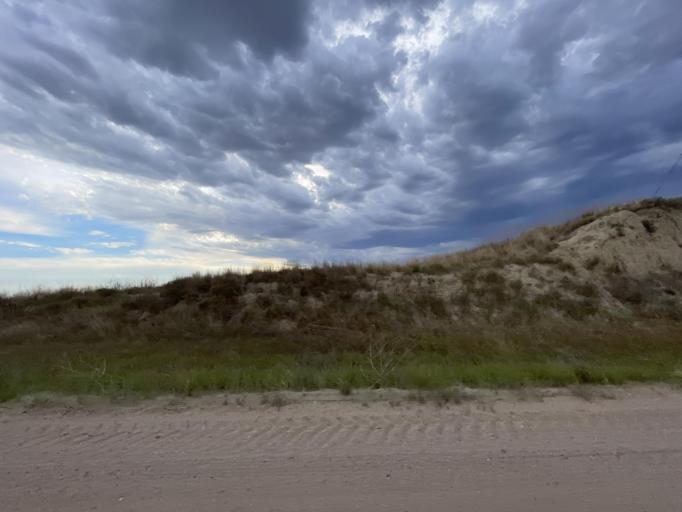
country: US
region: Nebraska
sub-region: Red Willow County
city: McCook
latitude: 40.2421
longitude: -100.7603
